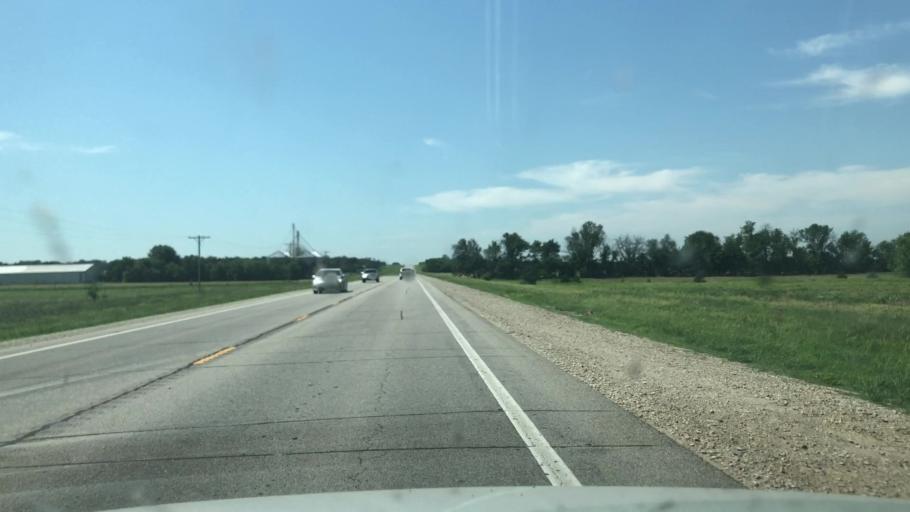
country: US
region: Kansas
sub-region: Butler County
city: Douglass
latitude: 37.3847
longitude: -97.0069
